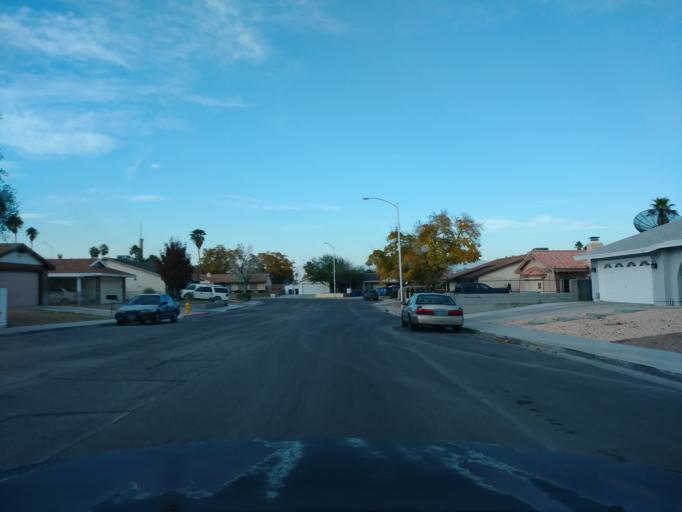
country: US
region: Nevada
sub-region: Clark County
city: Spring Valley
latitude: 36.1686
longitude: -115.2404
